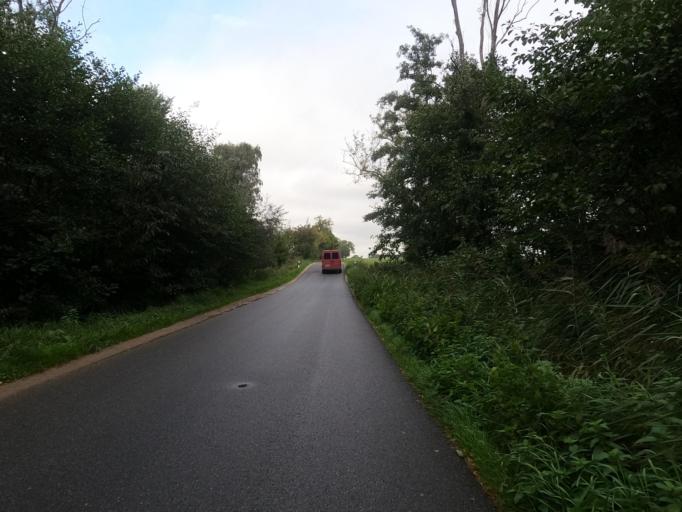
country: DE
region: Schleswig-Holstein
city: Neukirchen
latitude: 54.3116
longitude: 11.0414
